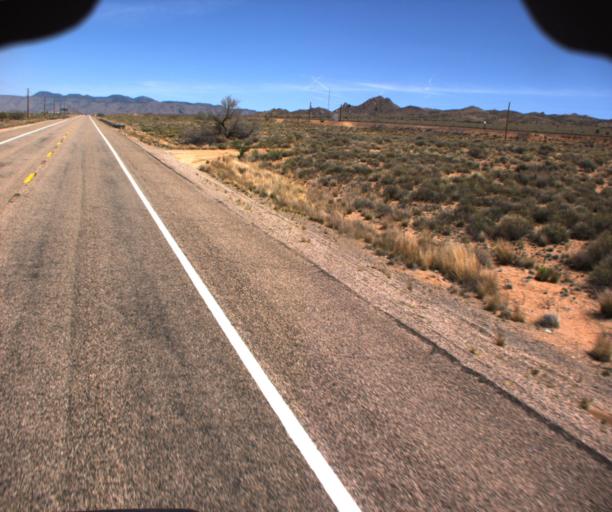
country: US
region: Arizona
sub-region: Mohave County
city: New Kingman-Butler
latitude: 35.3870
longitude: -113.8481
